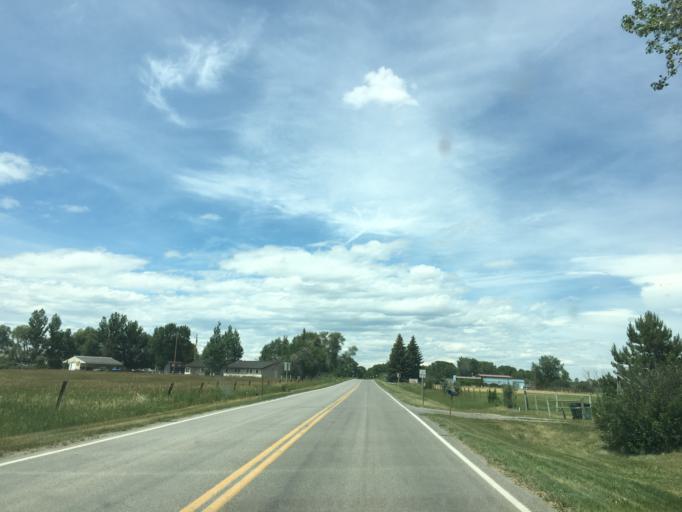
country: US
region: Montana
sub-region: Teton County
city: Choteau
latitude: 47.8261
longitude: -112.1946
